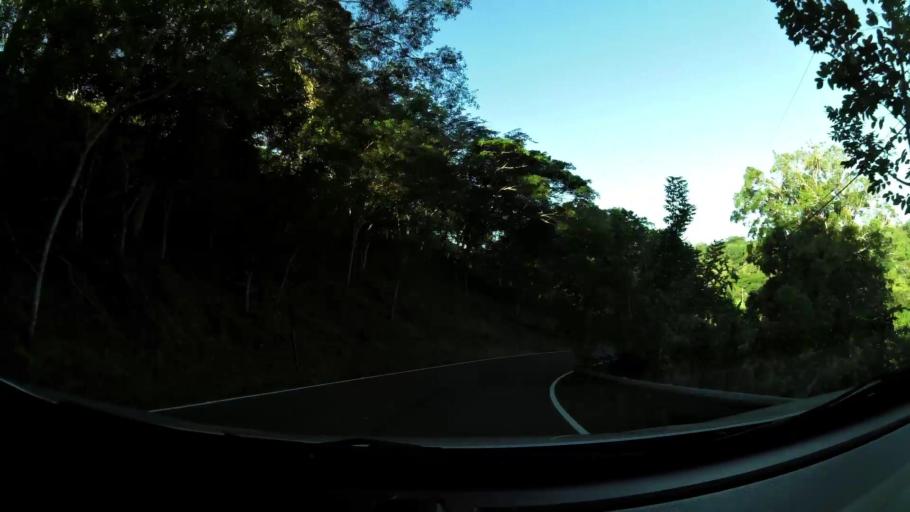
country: CR
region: Puntarenas
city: Miramar
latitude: 10.1263
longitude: -84.8316
